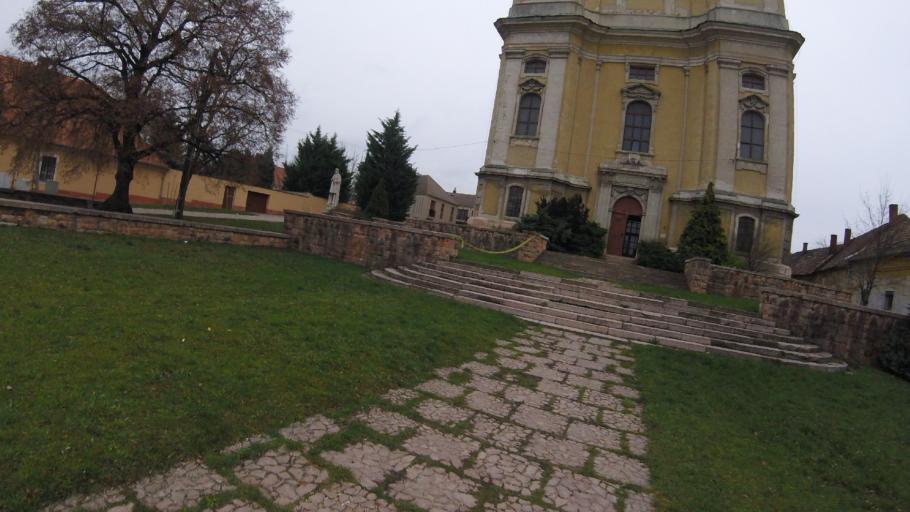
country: HU
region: Komarom-Esztergom
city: Tata
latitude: 47.6432
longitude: 18.3140
